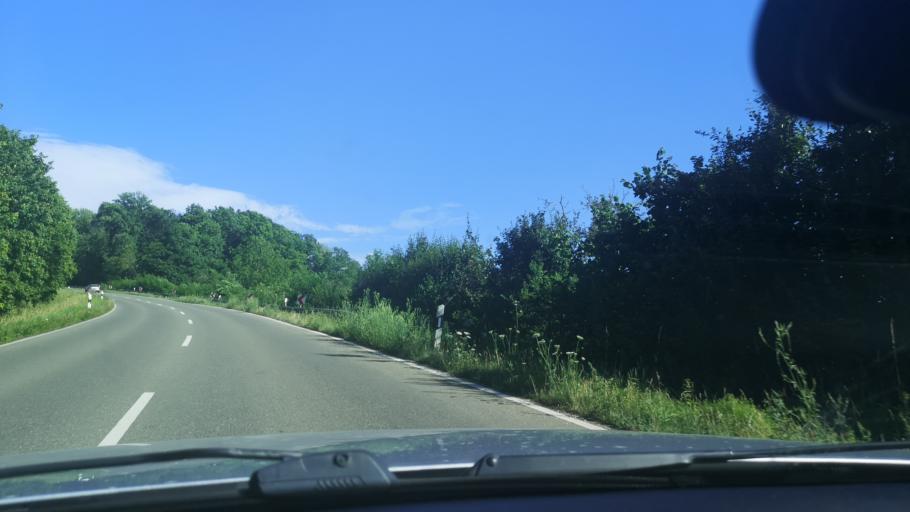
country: DE
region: Baden-Wuerttemberg
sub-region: Regierungsbezirk Stuttgart
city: Heiningen
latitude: 48.6631
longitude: 9.6279
